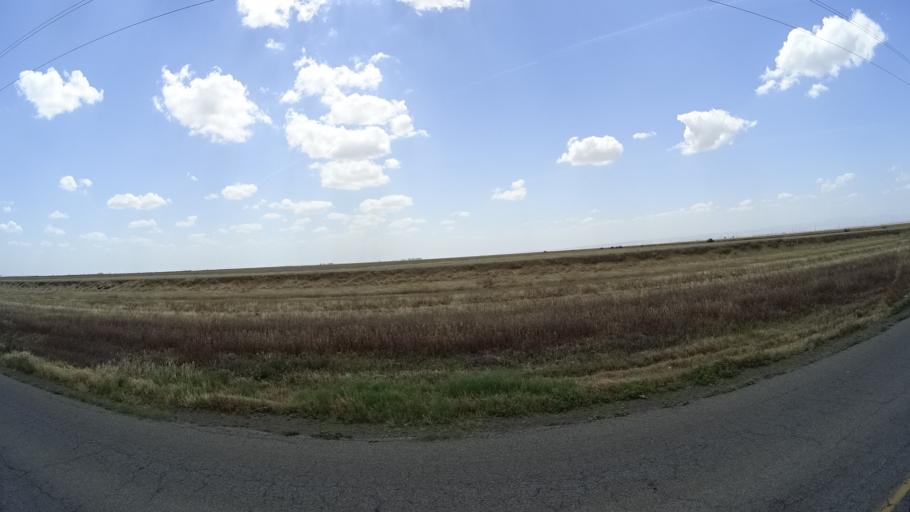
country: US
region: California
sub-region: Kings County
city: Stratford
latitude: 36.1896
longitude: -119.8941
